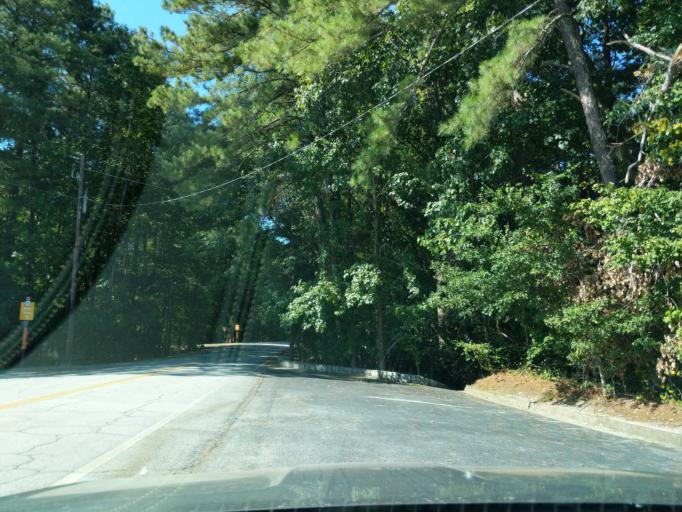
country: US
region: Georgia
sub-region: DeKalb County
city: Stone Mountain
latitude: 33.8191
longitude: -84.1513
